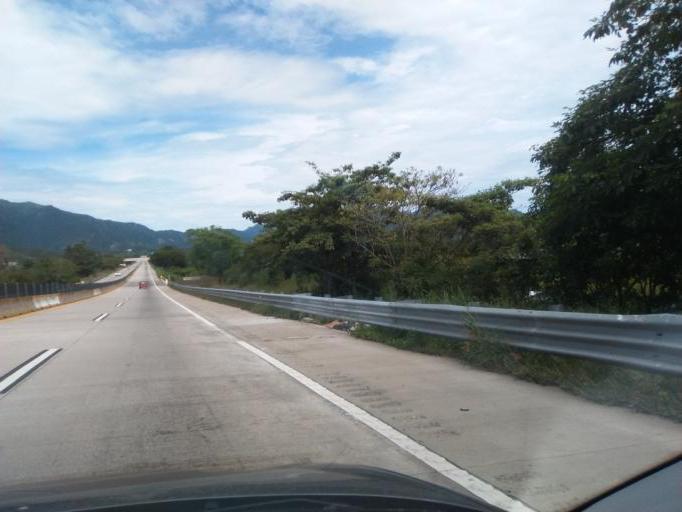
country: MX
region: Guerrero
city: El Ocotito
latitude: 17.2473
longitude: -99.5216
